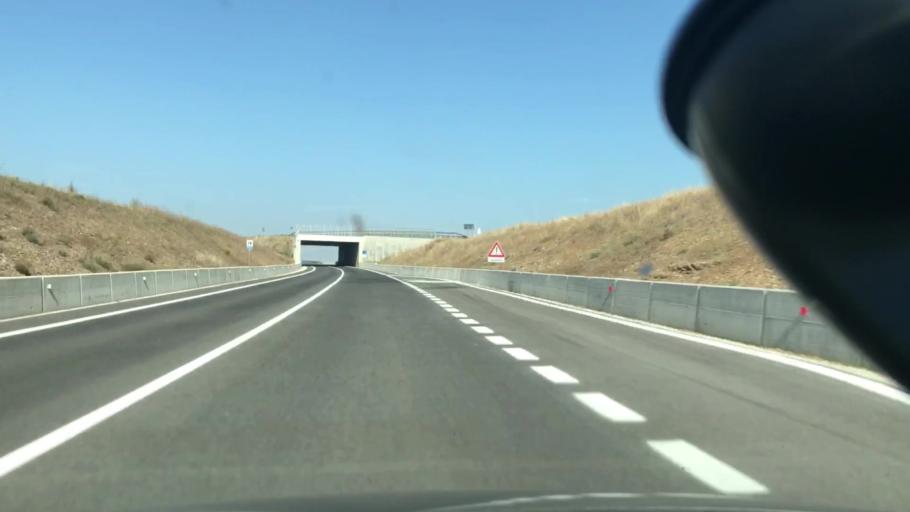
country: IT
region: Basilicate
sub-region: Provincia di Potenza
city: Palazzo San Gervasio
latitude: 40.9683
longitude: 16.0044
